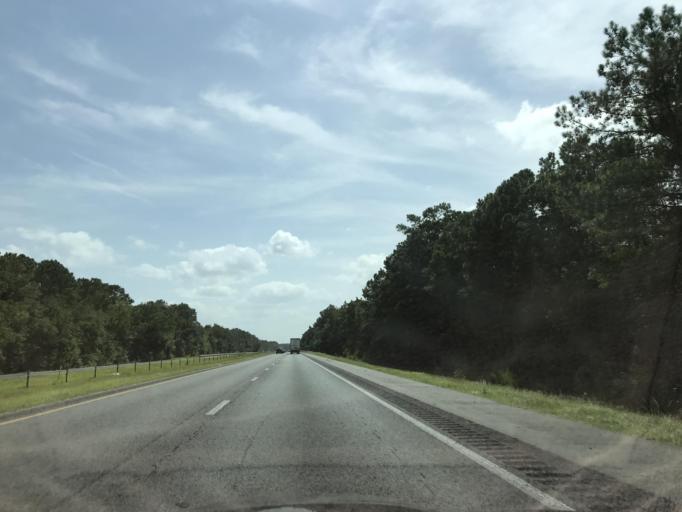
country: US
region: North Carolina
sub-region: Duplin County
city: Wallace
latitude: 34.7229
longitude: -77.9453
